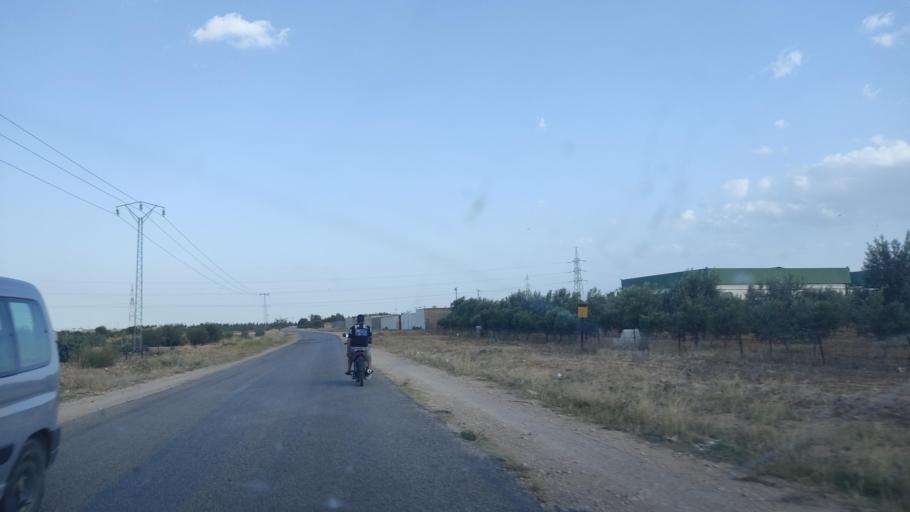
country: TN
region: Safaqis
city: Sfax
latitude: 34.8347
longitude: 10.6319
